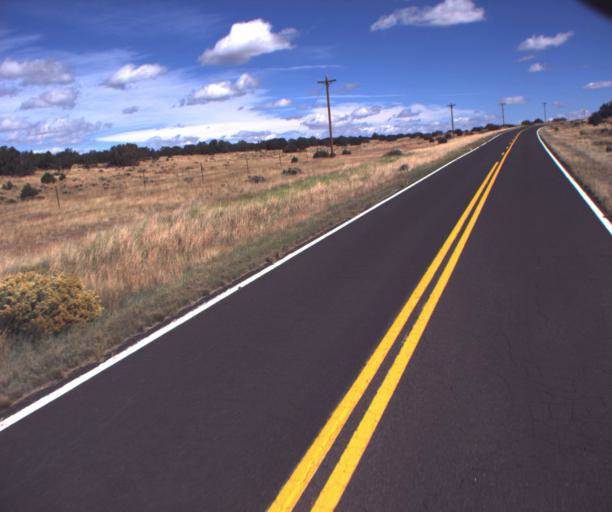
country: US
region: New Mexico
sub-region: McKinley County
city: Zuni Pueblo
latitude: 34.9864
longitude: -109.1193
